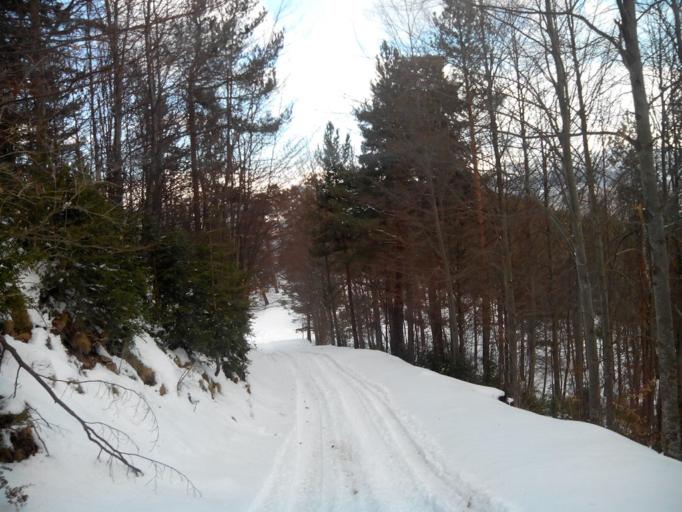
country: ES
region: Catalonia
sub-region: Provincia de Barcelona
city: Sant Julia de Cerdanyola
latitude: 42.2094
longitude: 1.9484
